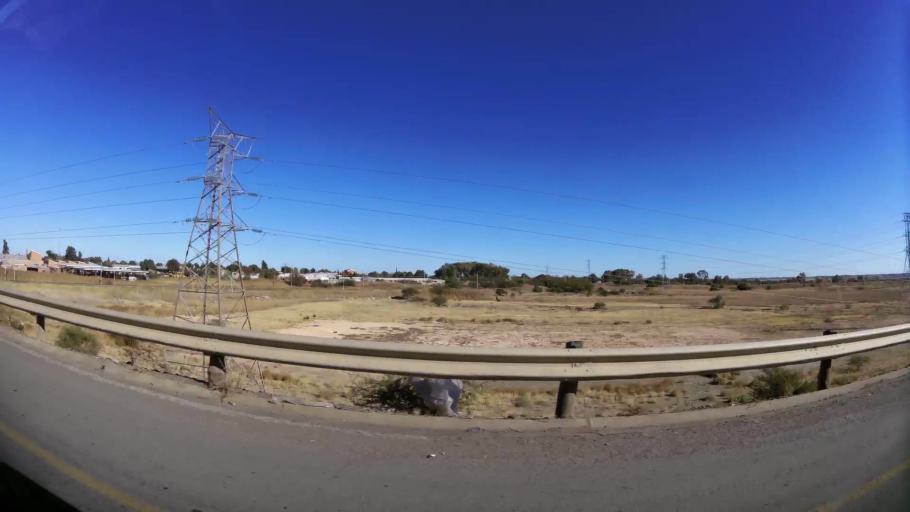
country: ZA
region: Northern Cape
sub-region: Frances Baard District Municipality
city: Kimberley
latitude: -28.7129
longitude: 24.7758
